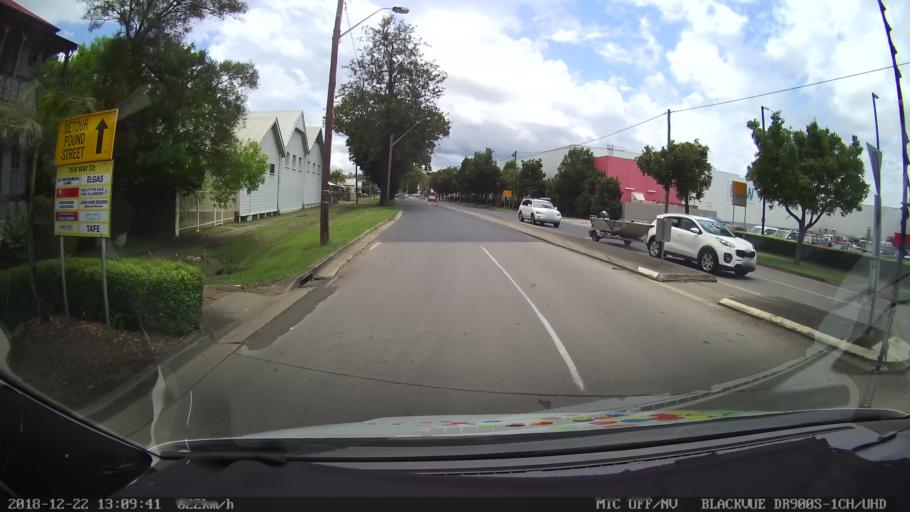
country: AU
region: New South Wales
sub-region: Clarence Valley
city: Grafton
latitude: -29.6918
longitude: 152.9383
